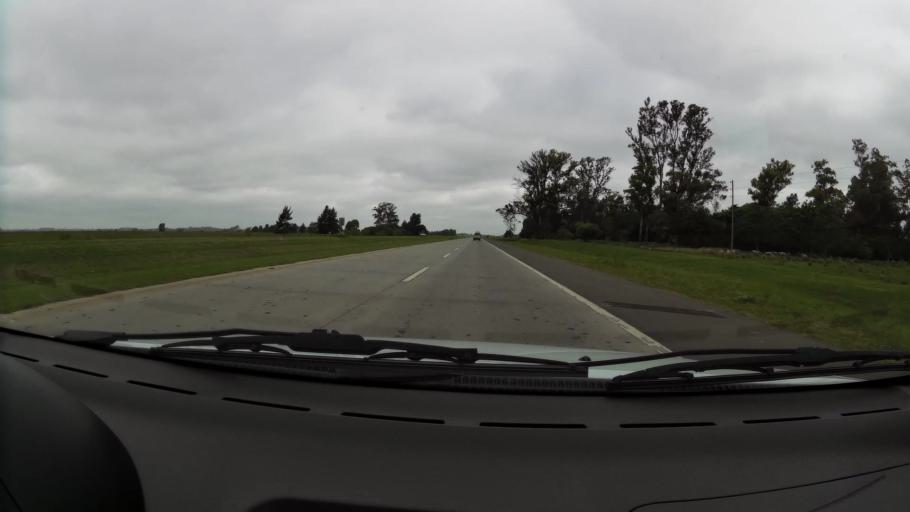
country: AR
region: Buenos Aires
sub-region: Partido de Brandsen
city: Brandsen
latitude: -35.0361
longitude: -58.1907
